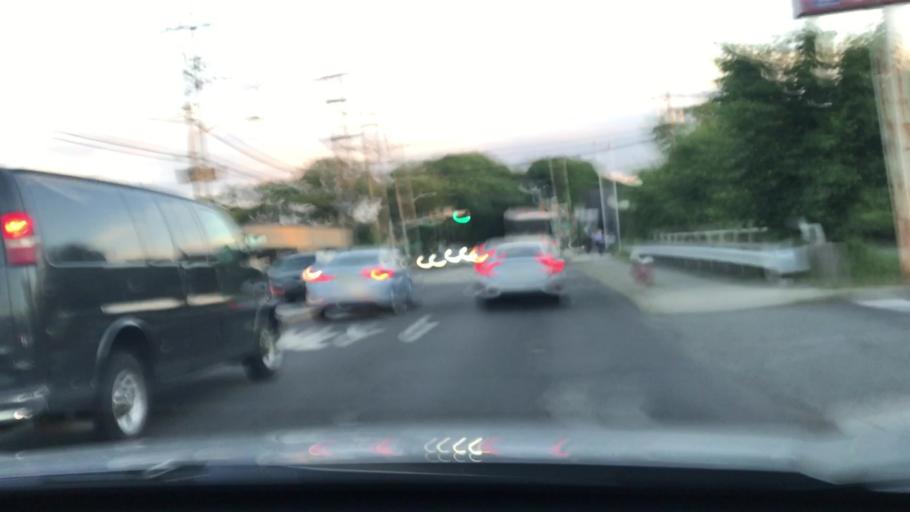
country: US
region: New Jersey
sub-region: Bergen County
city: Bergenfield
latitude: 40.9131
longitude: -73.9976
